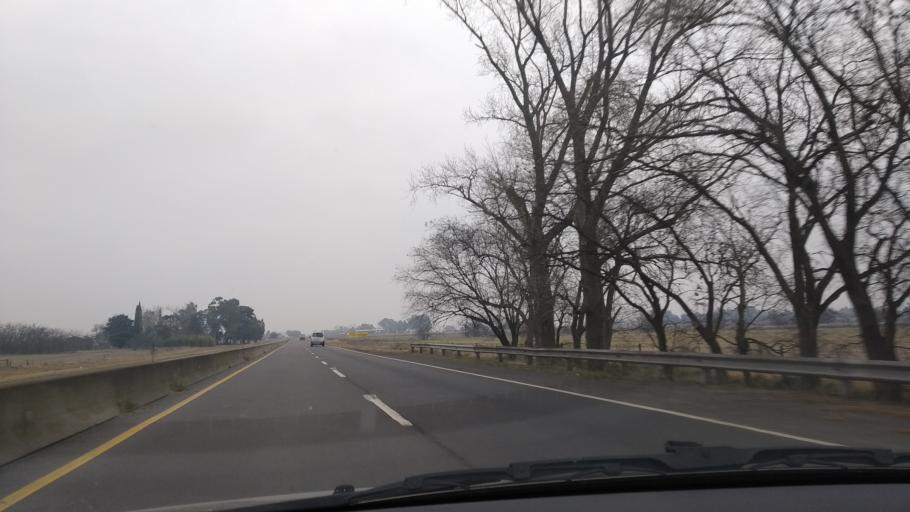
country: AR
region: Buenos Aires
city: Olavarria
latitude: -36.8718
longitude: -60.1355
